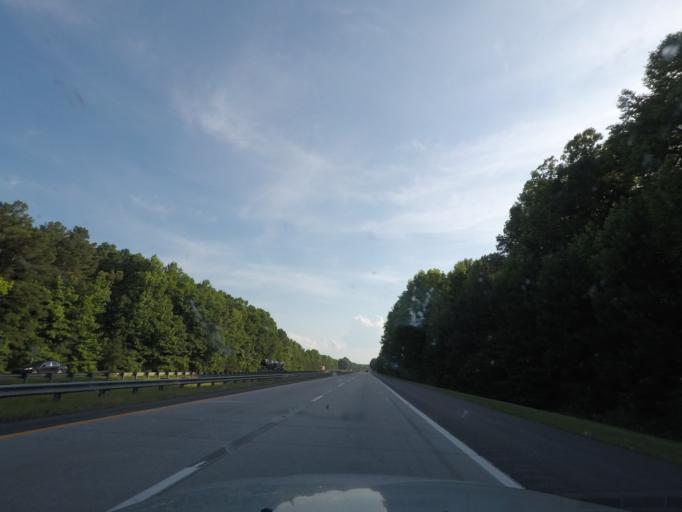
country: US
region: North Carolina
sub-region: Granville County
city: Oxford
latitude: 36.2429
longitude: -78.6324
